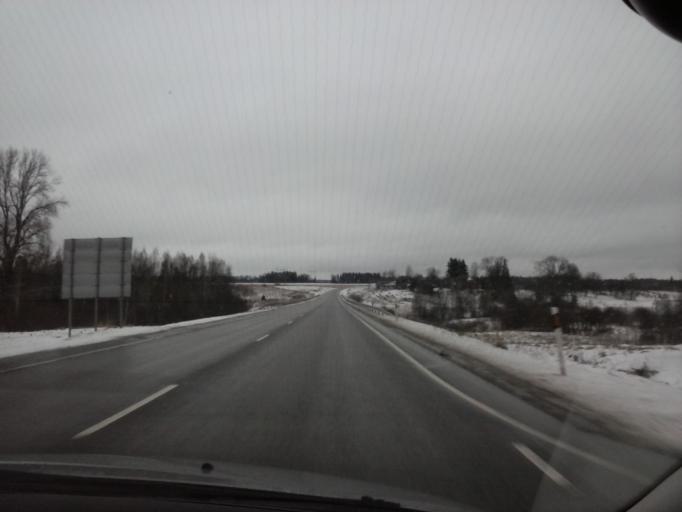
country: EE
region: Tartu
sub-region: Elva linn
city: Elva
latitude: 58.1914
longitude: 26.3509
